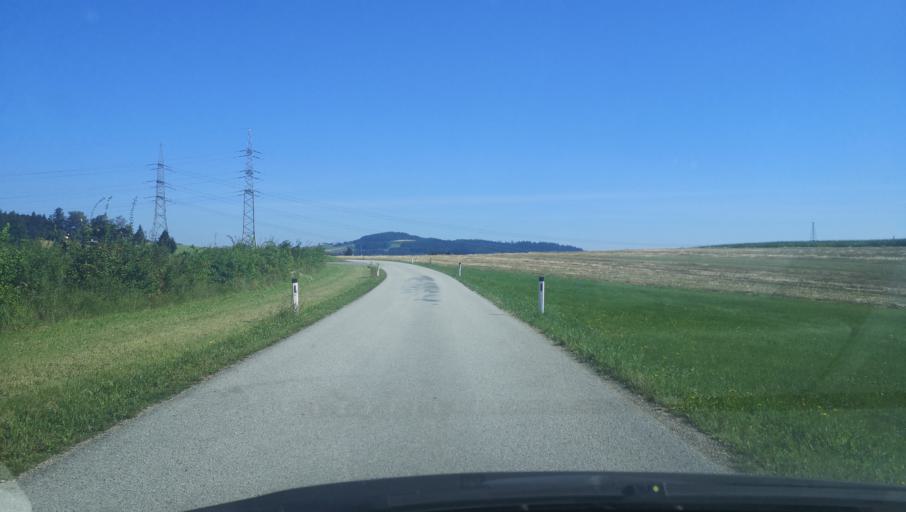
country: AT
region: Lower Austria
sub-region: Politischer Bezirk Melk
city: Blindenmarkt
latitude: 48.1468
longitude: 15.0009
